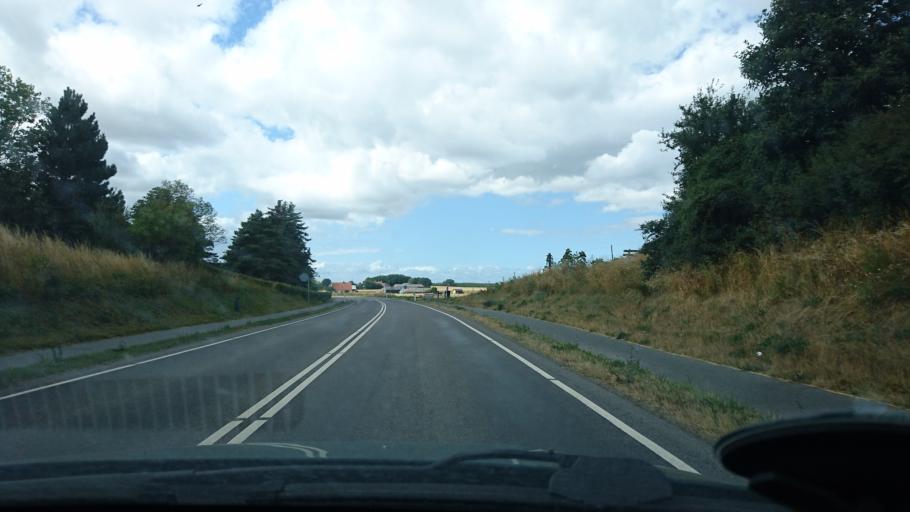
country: DK
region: Zealand
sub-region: Vordingborg Kommune
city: Stege
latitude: 54.9955
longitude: 12.3130
